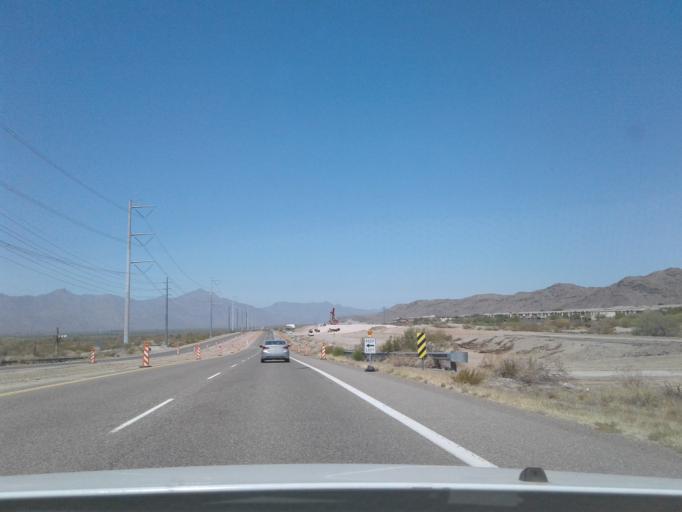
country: US
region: Arizona
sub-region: Maricopa County
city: Laveen
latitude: 33.2911
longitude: -112.0904
